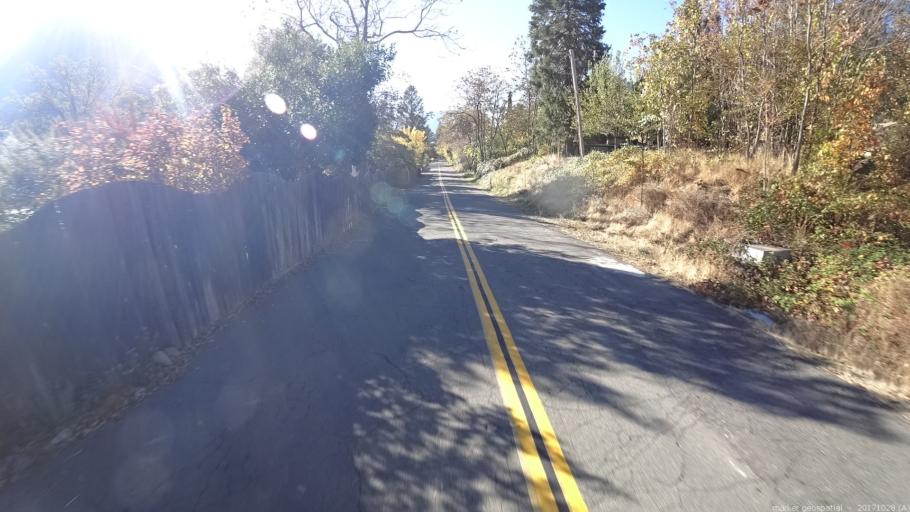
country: US
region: California
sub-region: Trinity County
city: Lewiston
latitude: 40.7064
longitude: -122.6369
